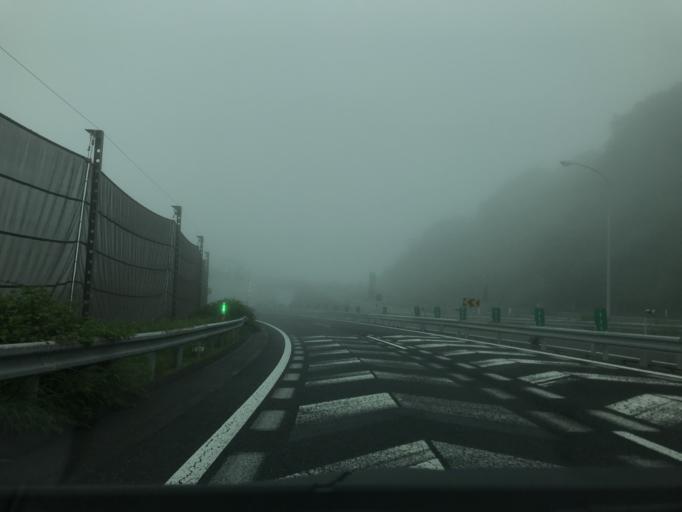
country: JP
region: Oita
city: Hiji
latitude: 33.3555
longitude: 131.4465
